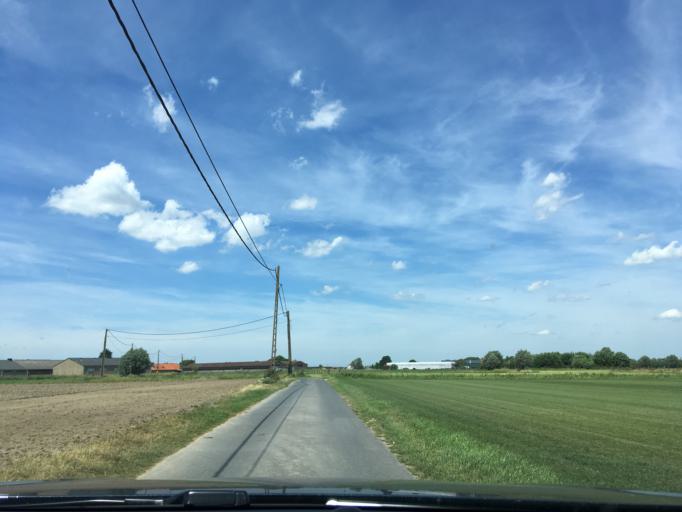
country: BE
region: Flanders
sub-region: Provincie West-Vlaanderen
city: Lichtervelde
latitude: 51.0205
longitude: 3.1861
